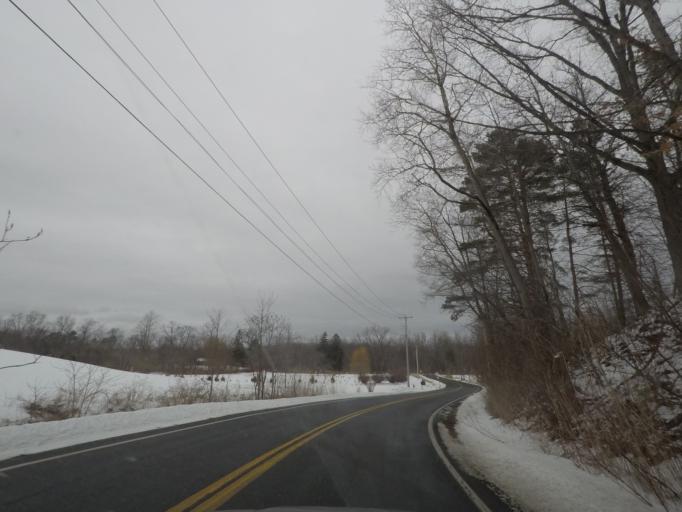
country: US
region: New York
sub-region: Schenectady County
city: Niskayuna
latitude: 42.7691
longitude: -73.8066
